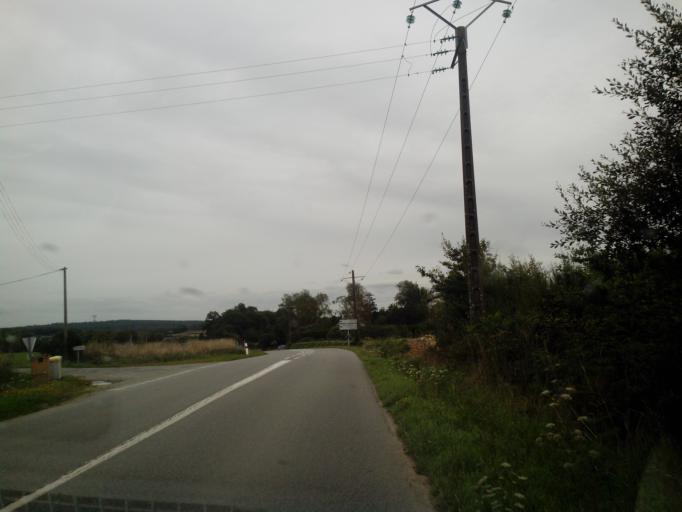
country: FR
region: Brittany
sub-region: Departement du Finistere
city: Arzano
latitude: 47.9038
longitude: -3.4332
